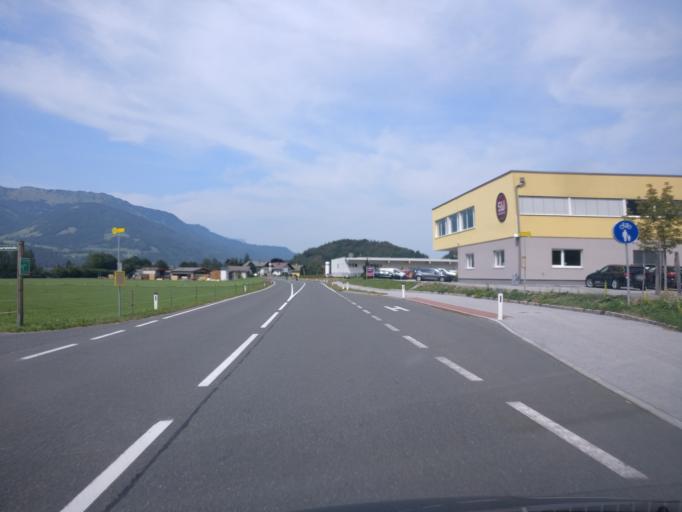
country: AT
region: Salzburg
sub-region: Politischer Bezirk Hallein
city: Golling an der Salzach
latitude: 47.5870
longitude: 13.1792
